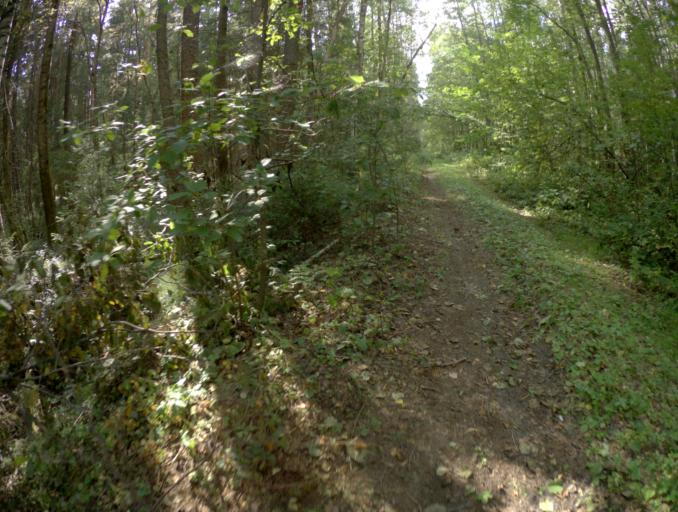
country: RU
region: Vladimir
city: Sobinka
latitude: 55.9166
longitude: 40.0906
